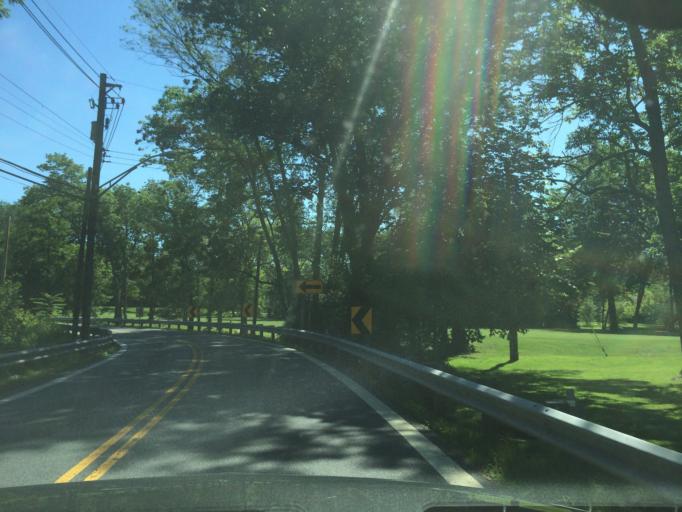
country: US
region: Maryland
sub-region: Baltimore County
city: Garrison
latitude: 39.4085
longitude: -76.7429
